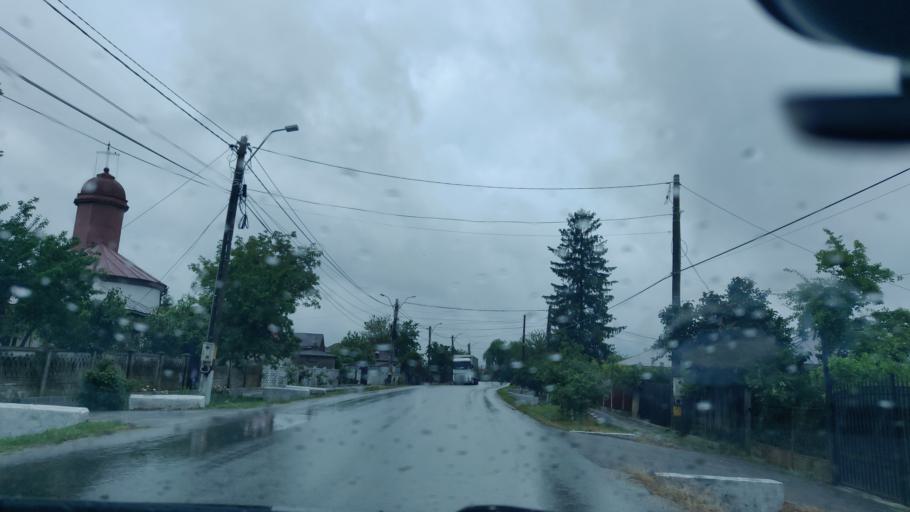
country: RO
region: Giurgiu
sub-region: Comuna Bulbucata
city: Bulbucata
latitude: 44.2816
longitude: 25.8114
